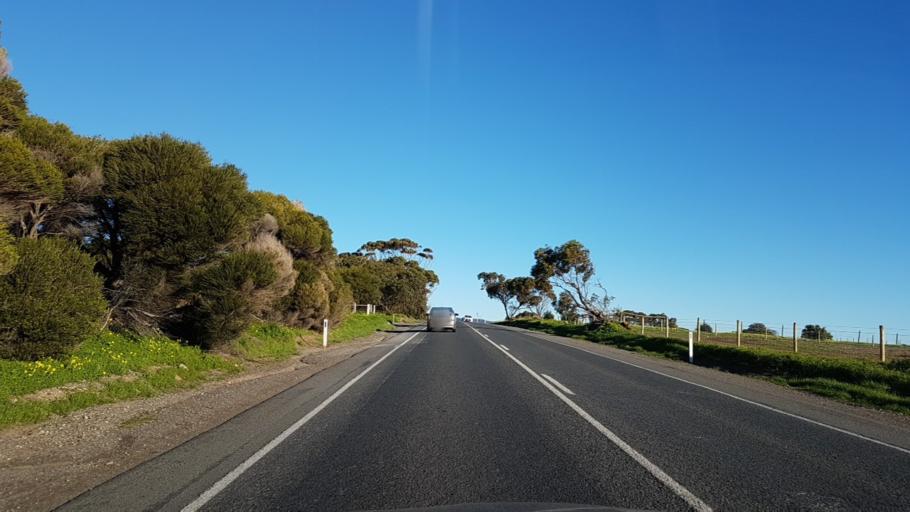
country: AU
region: South Australia
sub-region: Onkaparinga
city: Aldinga
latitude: -35.2476
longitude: 138.4945
